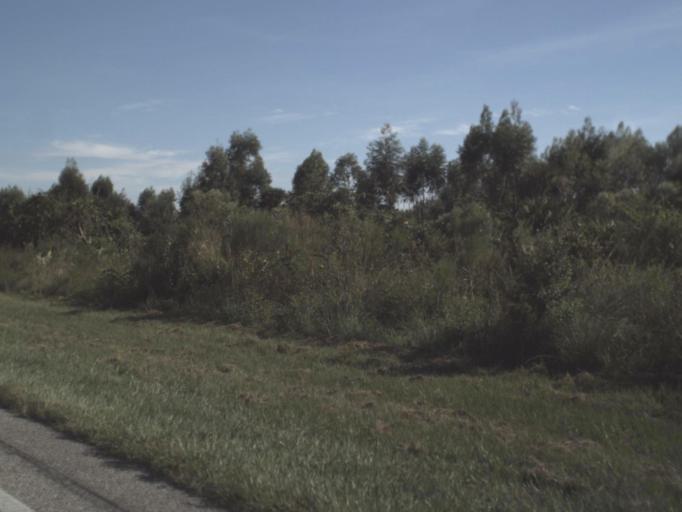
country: US
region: Florida
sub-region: Glades County
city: Moore Haven
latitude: 26.9048
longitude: -81.2597
